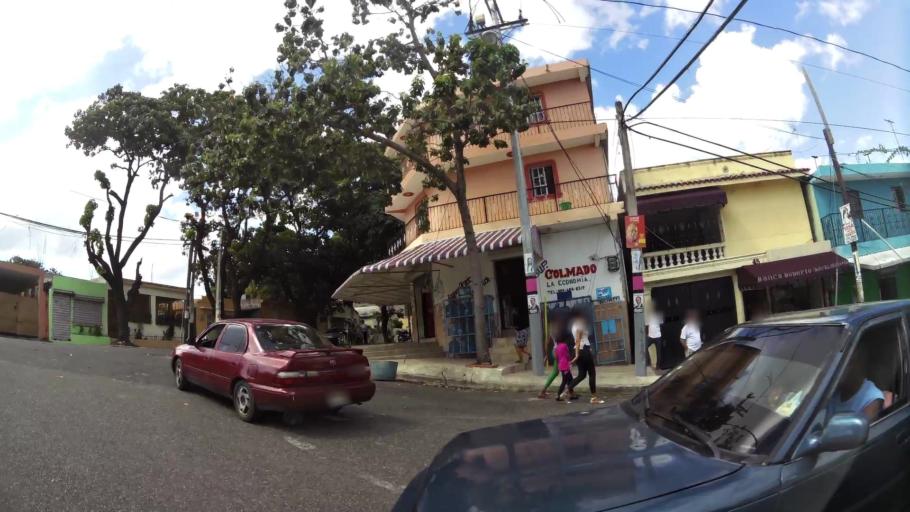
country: DO
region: Nacional
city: Ensanche Luperon
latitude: 18.4962
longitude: -69.8887
